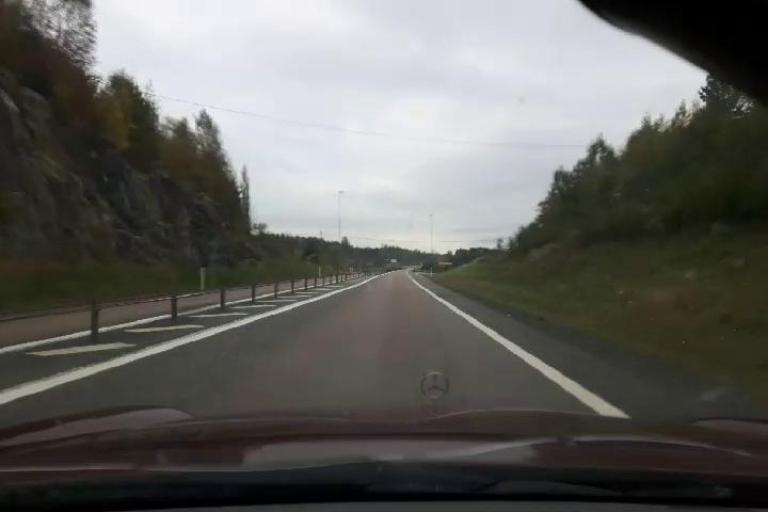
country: SE
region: Vaesternorrland
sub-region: Kramfors Kommun
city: Nordingra
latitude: 62.9234
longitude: 18.0992
